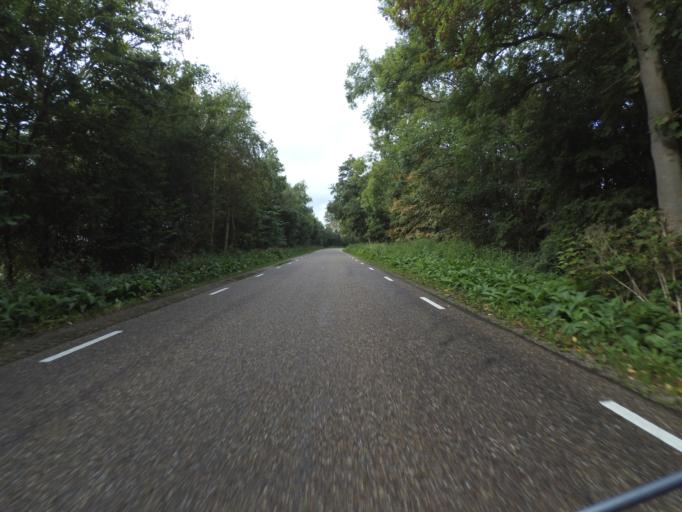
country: NL
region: North Holland
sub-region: Gemeente Hollands Kroon
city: Den Oever
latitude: 52.8642
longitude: 4.9231
